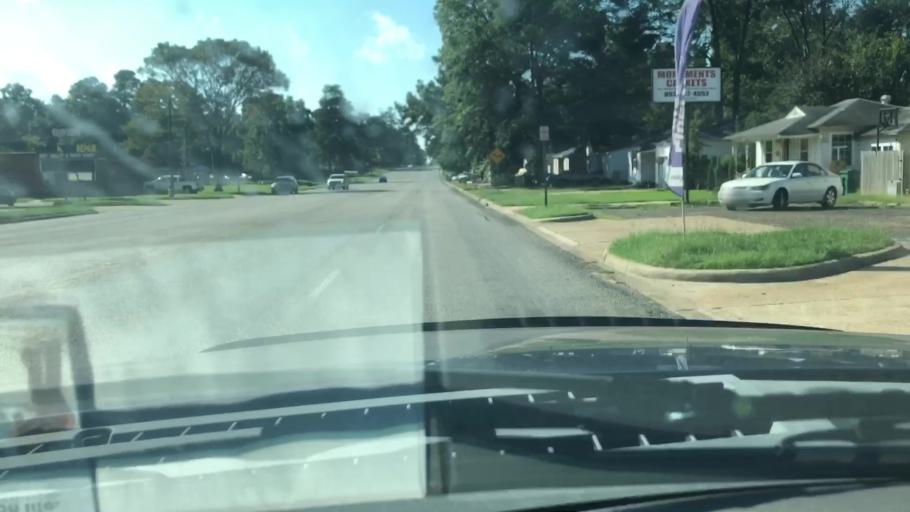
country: US
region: Arkansas
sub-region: Miller County
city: Texarkana
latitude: 33.4479
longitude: -94.0531
